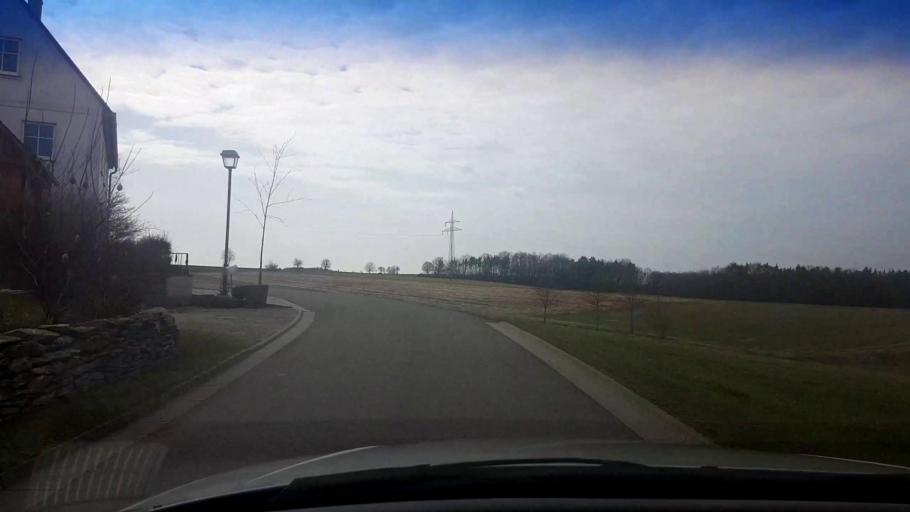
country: DE
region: Bavaria
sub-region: Upper Franconia
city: Burgebrach
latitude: 49.8057
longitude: 10.7770
